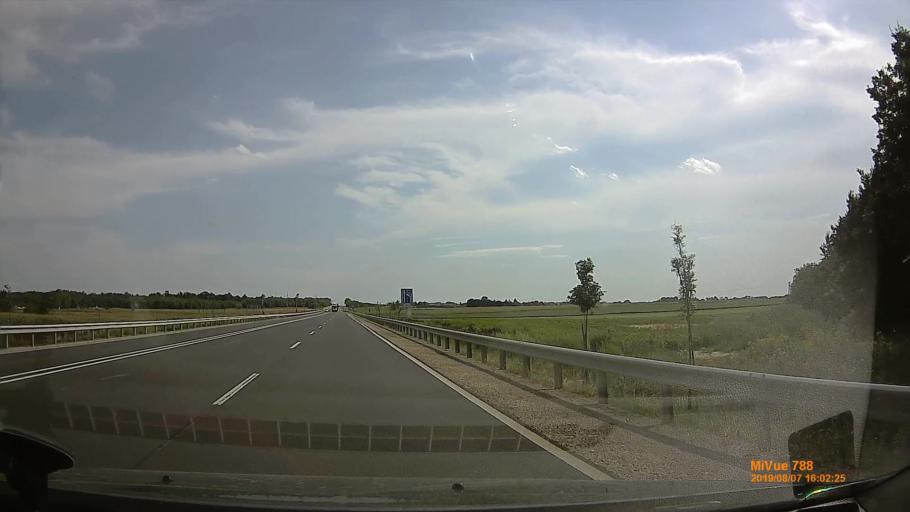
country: HU
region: Vas
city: Kormend
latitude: 46.9788
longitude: 16.6252
